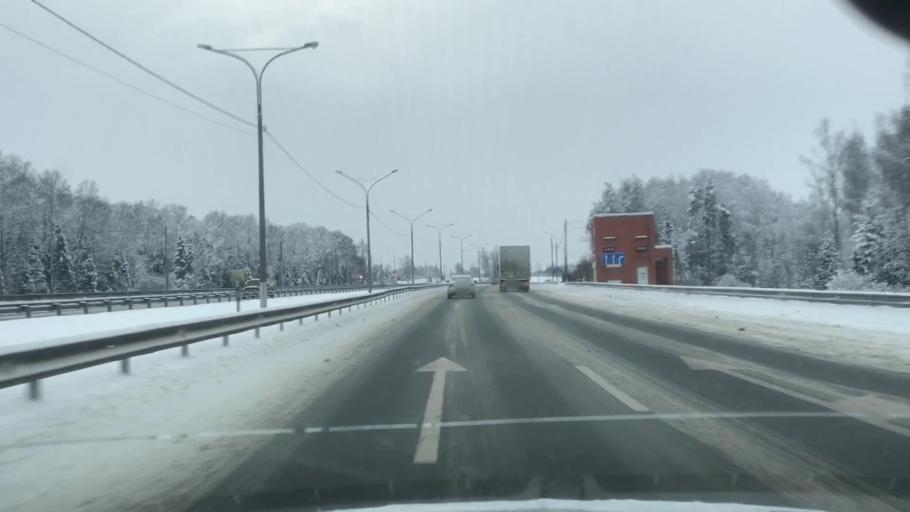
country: RU
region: Moskovskaya
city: Mikhnevo
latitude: 55.1316
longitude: 37.9342
